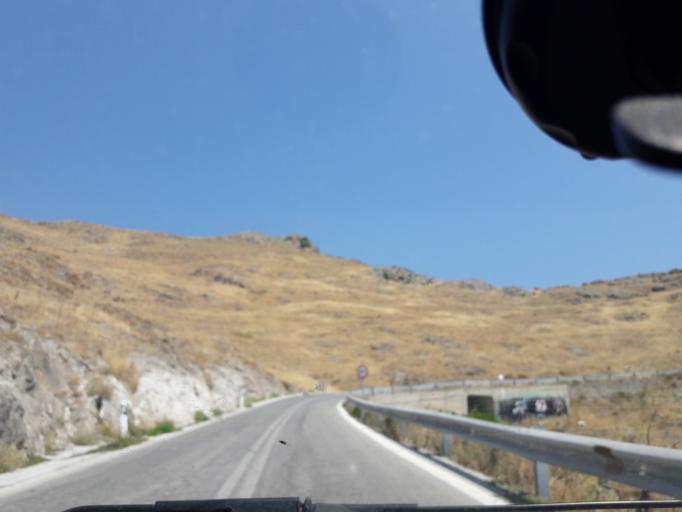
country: GR
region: North Aegean
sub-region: Nomos Lesvou
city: Myrina
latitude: 39.8632
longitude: 25.0777
